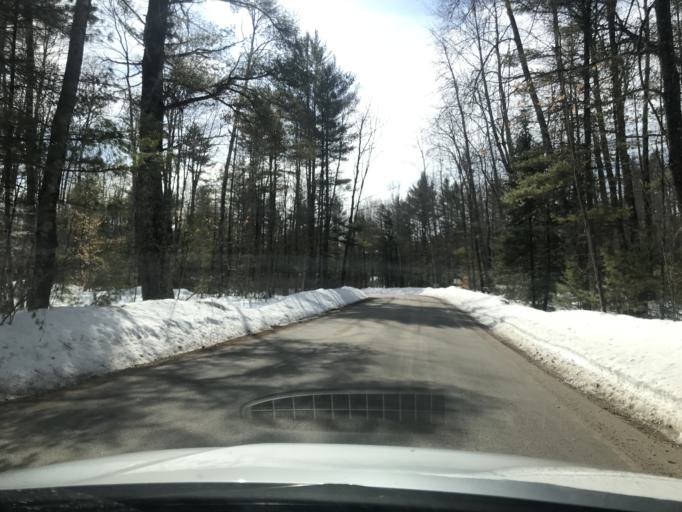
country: US
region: Wisconsin
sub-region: Menominee County
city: Legend Lake
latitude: 45.1180
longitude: -88.4464
